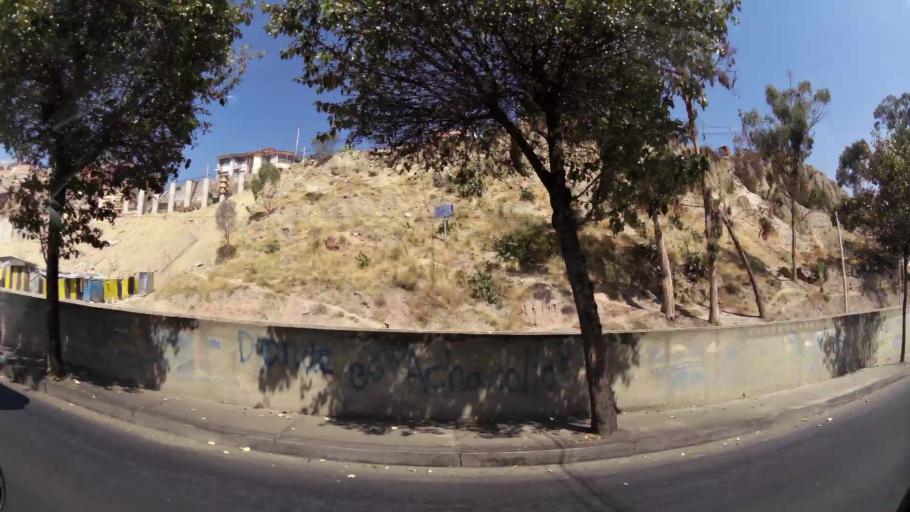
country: BO
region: La Paz
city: La Paz
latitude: -16.5455
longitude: -68.0856
